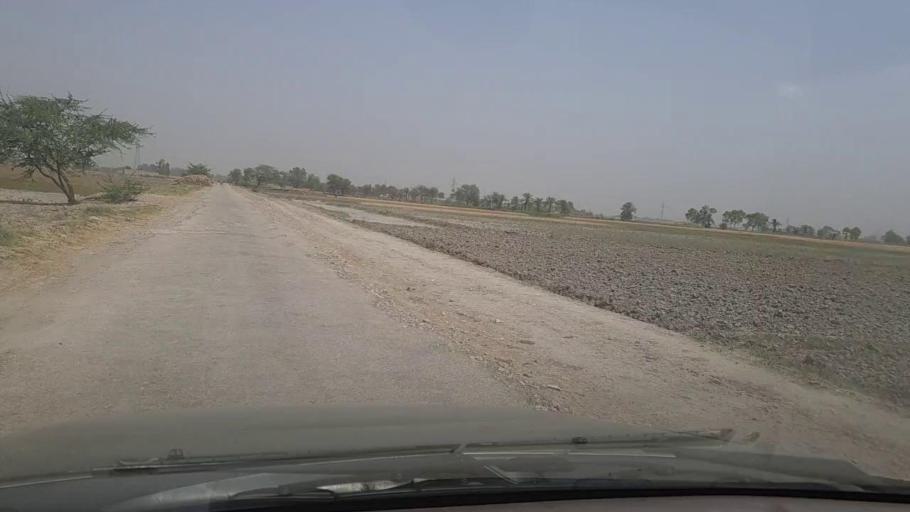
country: PK
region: Sindh
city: Madeji
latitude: 27.8203
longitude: 68.3966
